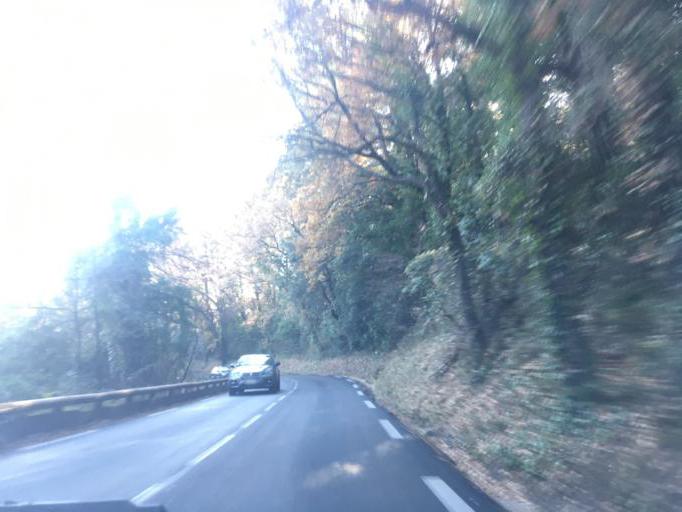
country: FR
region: Provence-Alpes-Cote d'Azur
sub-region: Departement du Var
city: Flayosc
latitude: 43.5362
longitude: 6.4001
